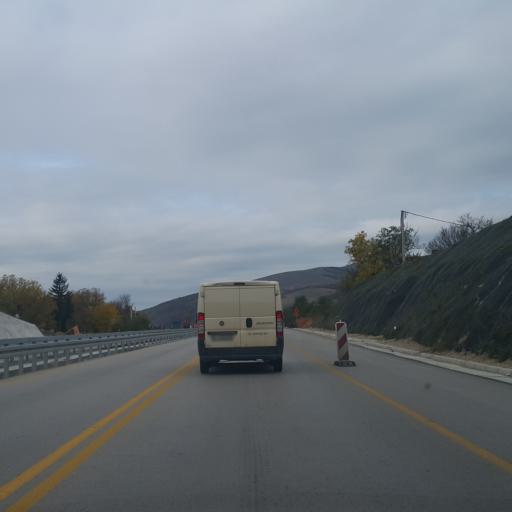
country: RS
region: Central Serbia
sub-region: Pirotski Okrug
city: Bela Palanka
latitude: 43.2206
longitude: 22.4091
